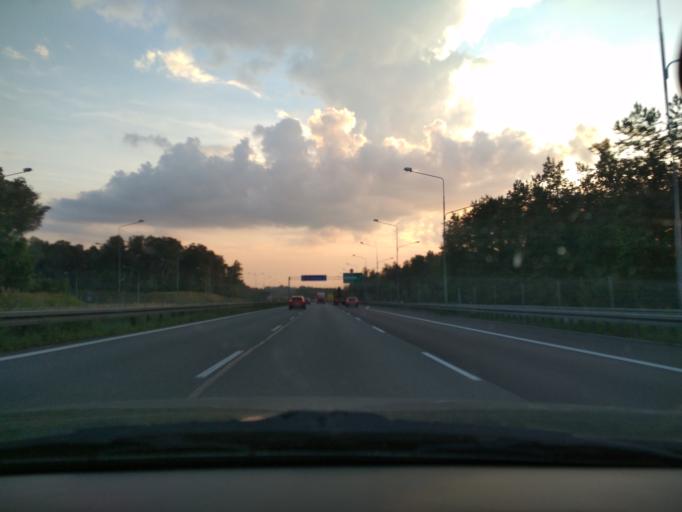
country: PL
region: Silesian Voivodeship
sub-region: Swietochlowice
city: Swietochlowice
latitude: 50.2551
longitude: 18.9503
